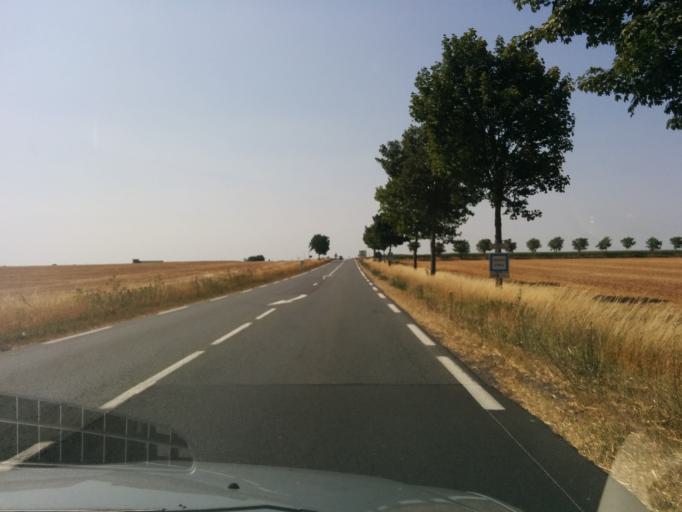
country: FR
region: Poitou-Charentes
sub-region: Departement de la Vienne
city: Neuville-de-Poitou
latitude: 46.6918
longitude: 0.2564
